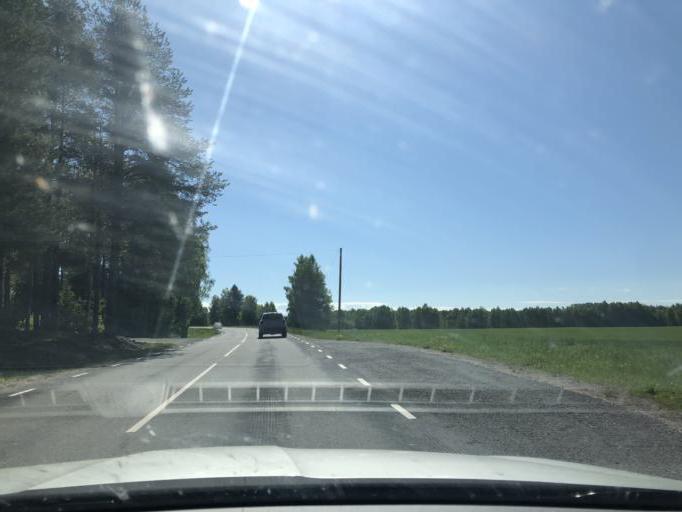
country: SE
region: Norrbotten
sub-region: Lulea Kommun
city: Gammelstad
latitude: 65.6583
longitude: 21.9953
